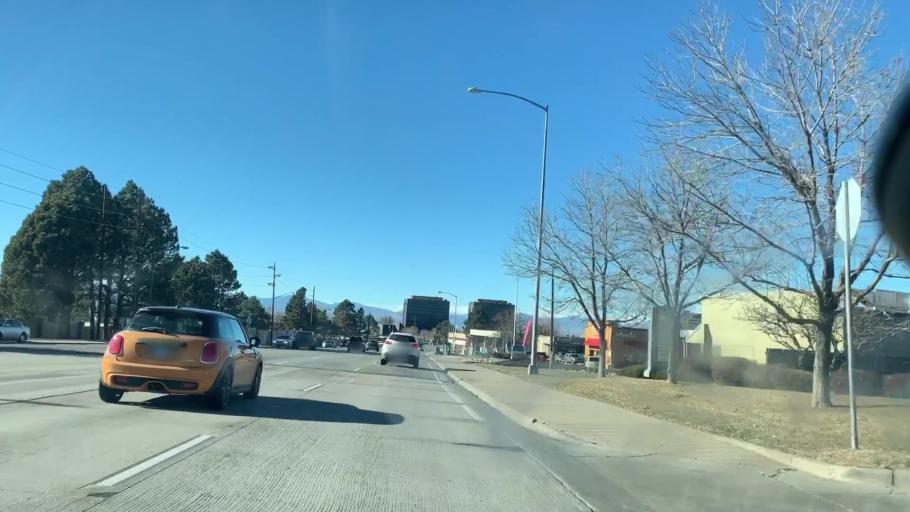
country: US
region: Colorado
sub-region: Adams County
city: Aurora
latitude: 39.6596
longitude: -104.8502
